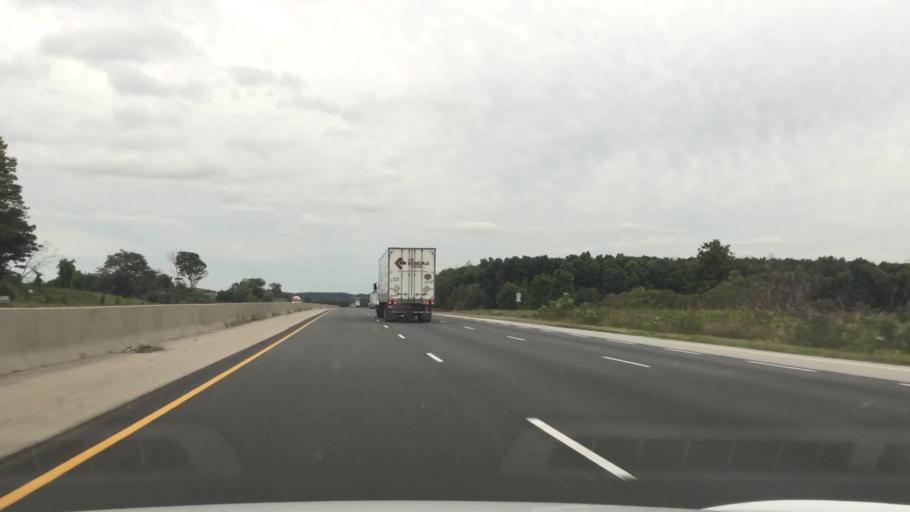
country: CA
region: Ontario
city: Kitchener
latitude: 43.3247
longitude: -80.4574
